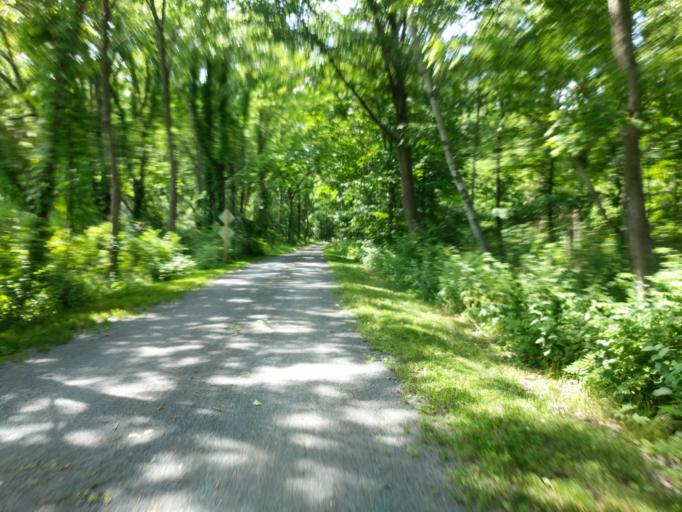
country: US
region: New York
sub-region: Tompkins County
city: Northwest Ithaca
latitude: 42.5186
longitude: -76.5741
